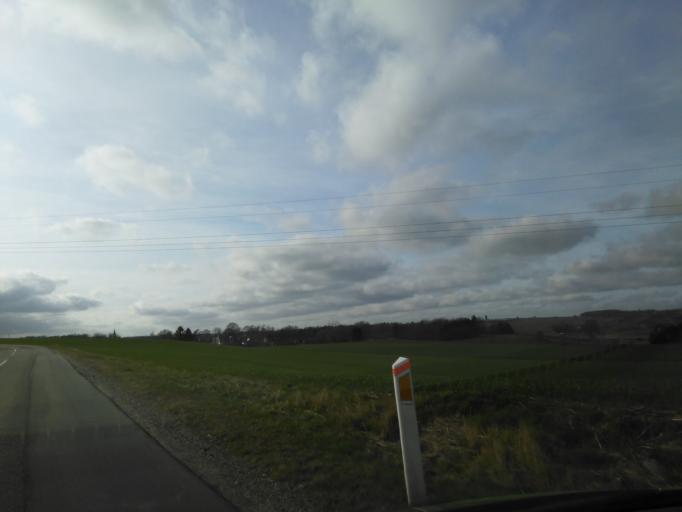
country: DK
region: Central Jutland
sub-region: Arhus Kommune
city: Framlev
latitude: 56.1692
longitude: 10.0493
